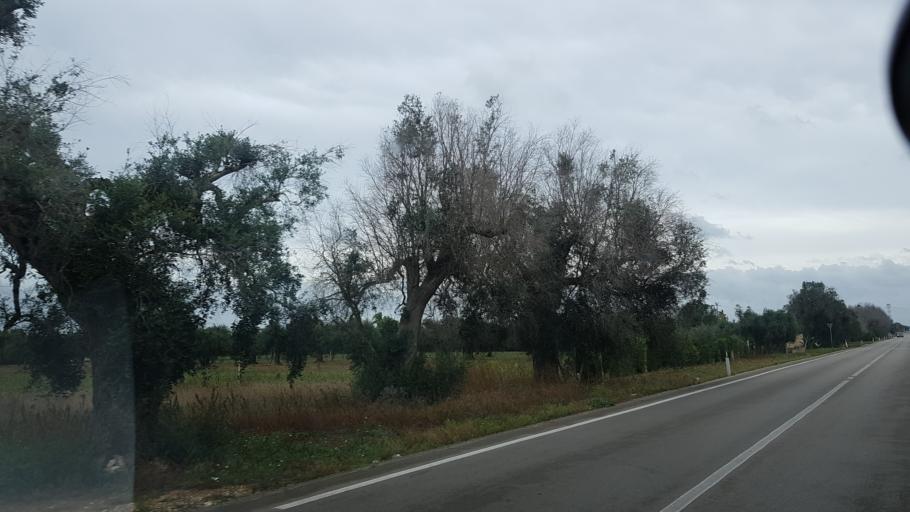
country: IT
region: Apulia
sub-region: Provincia di Lecce
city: Guagnano
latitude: 40.4008
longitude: 17.9644
